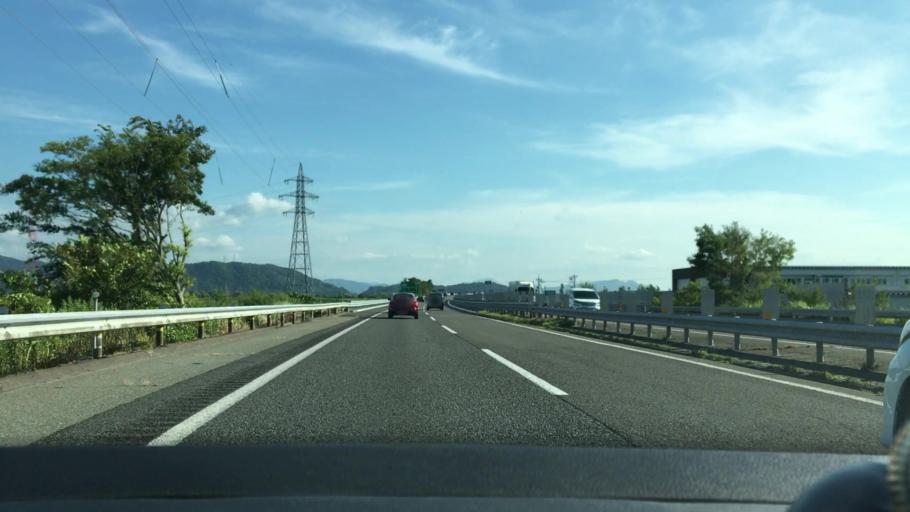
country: JP
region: Fukui
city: Maruoka
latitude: 36.1078
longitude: 136.2813
